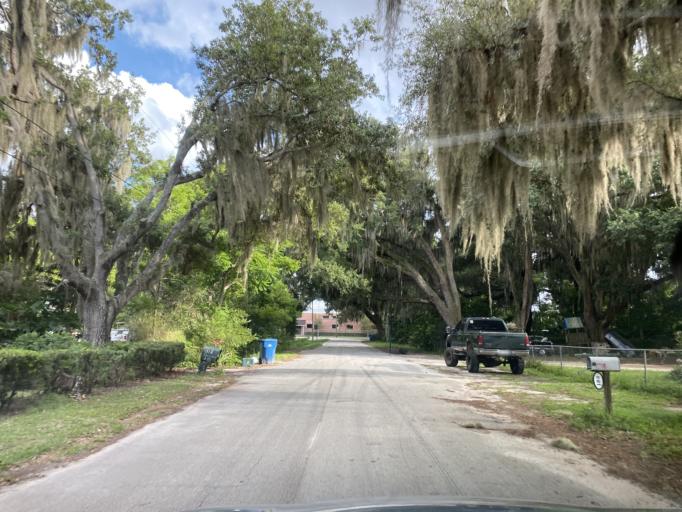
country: US
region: Florida
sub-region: Volusia County
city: Deltona
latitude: 28.8705
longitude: -81.2637
